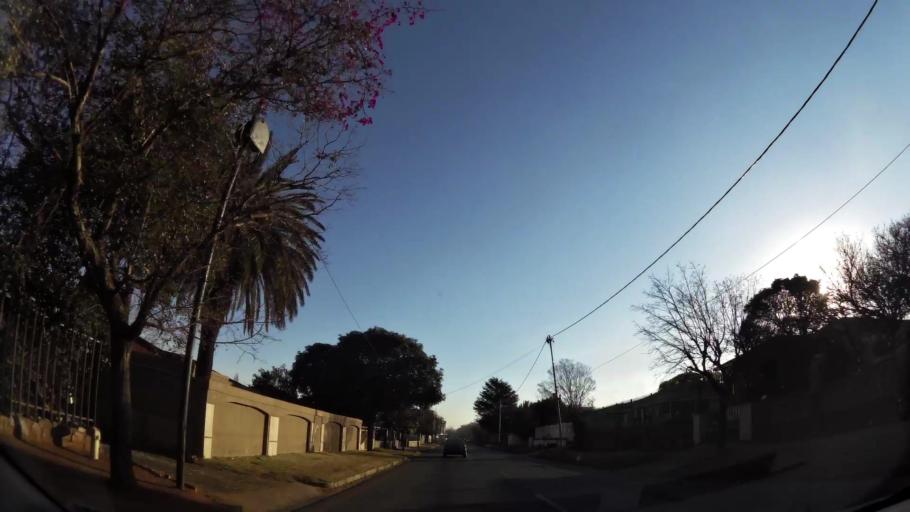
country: ZA
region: Gauteng
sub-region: City of Johannesburg Metropolitan Municipality
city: Roodepoort
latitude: -26.1771
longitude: 27.9320
